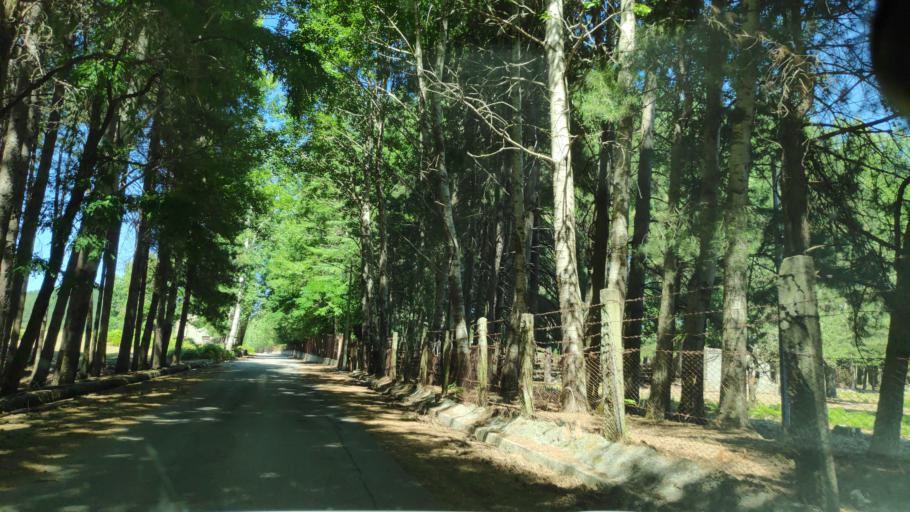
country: IT
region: Calabria
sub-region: Provincia di Reggio Calabria
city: Bova
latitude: 38.0286
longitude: 15.9442
